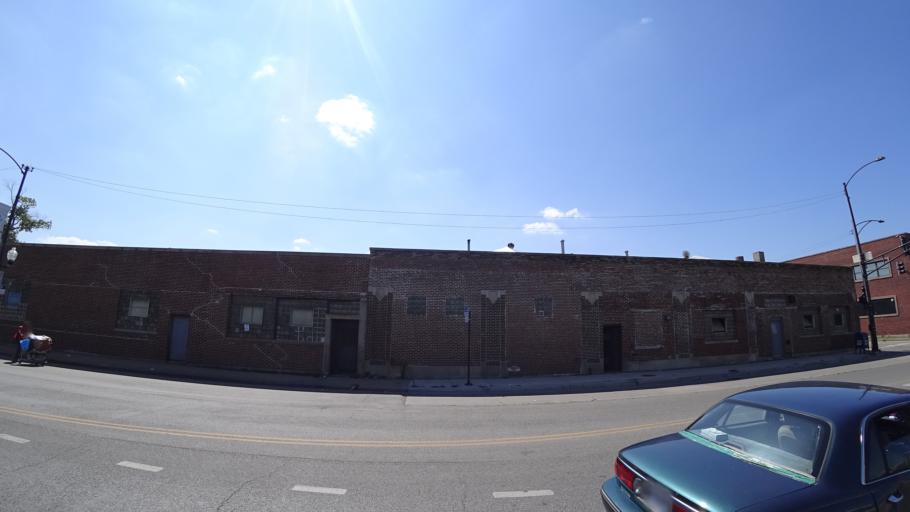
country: US
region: Illinois
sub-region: Cook County
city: Cicero
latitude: 41.8661
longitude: -87.7345
